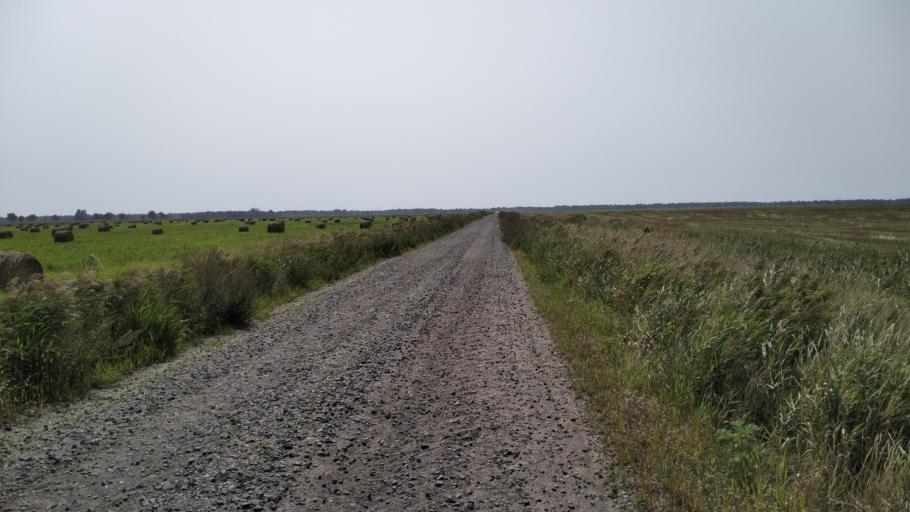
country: BY
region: Brest
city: Davyd-Haradok
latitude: 51.9927
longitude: 27.1761
